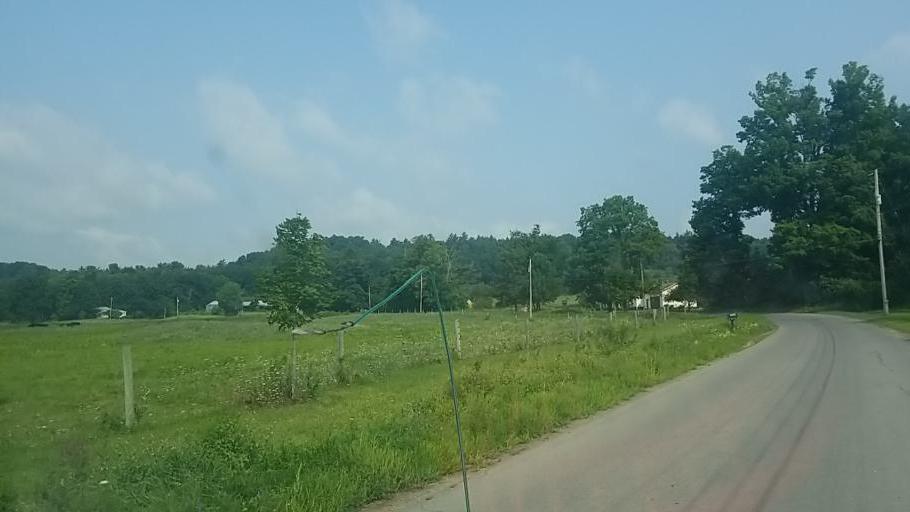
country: US
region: New York
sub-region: Montgomery County
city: Fonda
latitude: 42.9477
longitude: -74.4321
